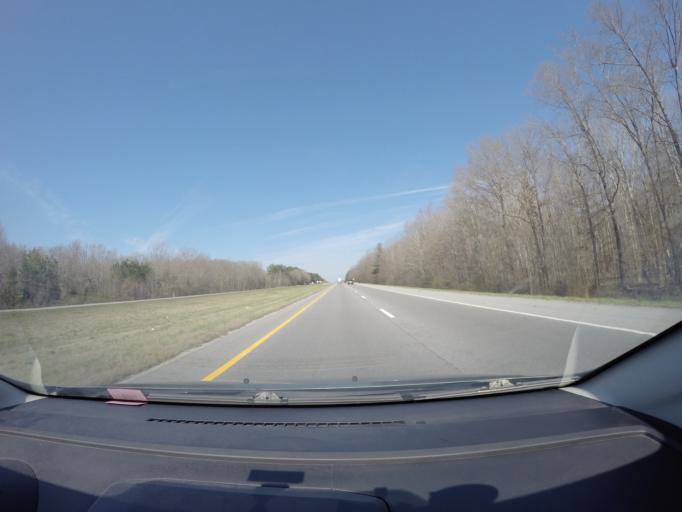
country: US
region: Tennessee
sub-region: Coffee County
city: Manchester
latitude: 35.5042
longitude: -86.0954
